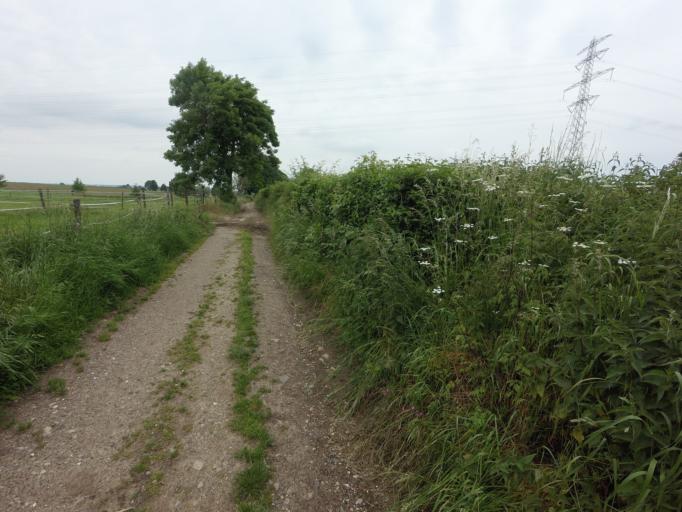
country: NL
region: Limburg
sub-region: Gemeente Voerendaal
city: Ubachsberg
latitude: 50.8557
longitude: 5.9535
